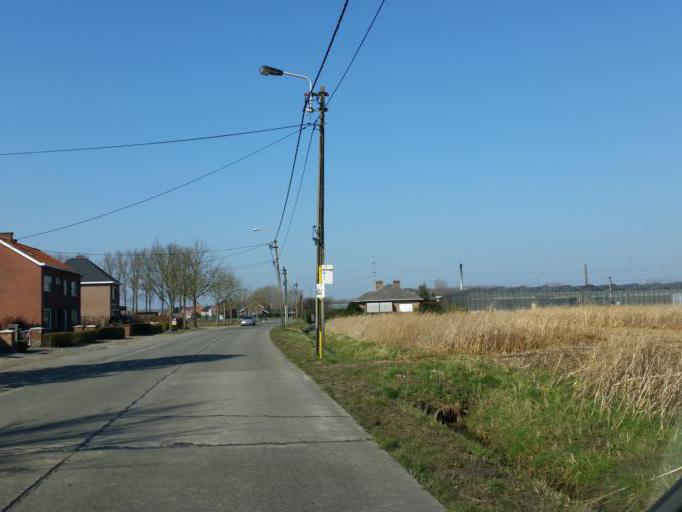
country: BE
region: Flanders
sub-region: Provincie Oost-Vlaanderen
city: Wachtebeke
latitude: 51.1302
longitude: 3.8794
